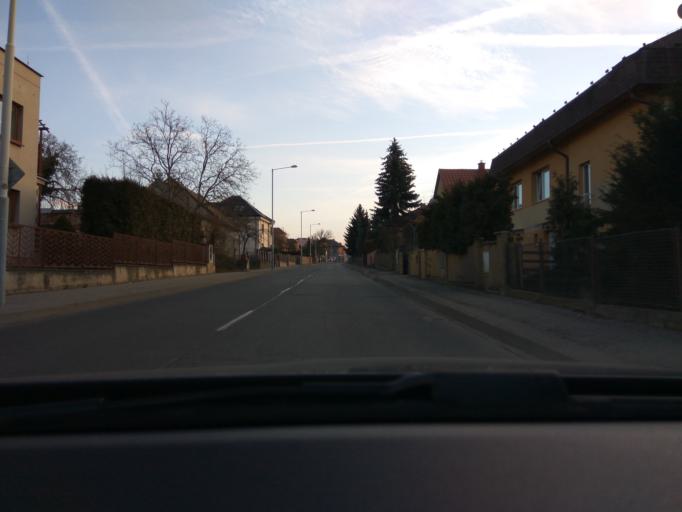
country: CZ
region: Praha
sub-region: Praha 18
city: Letnany
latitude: 50.1542
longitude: 14.5224
